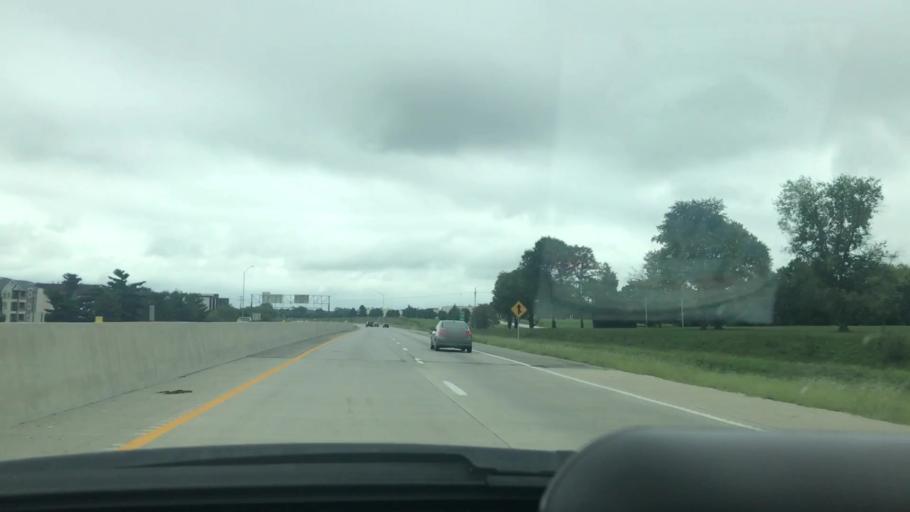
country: US
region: Missouri
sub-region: Jasper County
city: Duquesne
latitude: 37.0464
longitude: -94.4767
